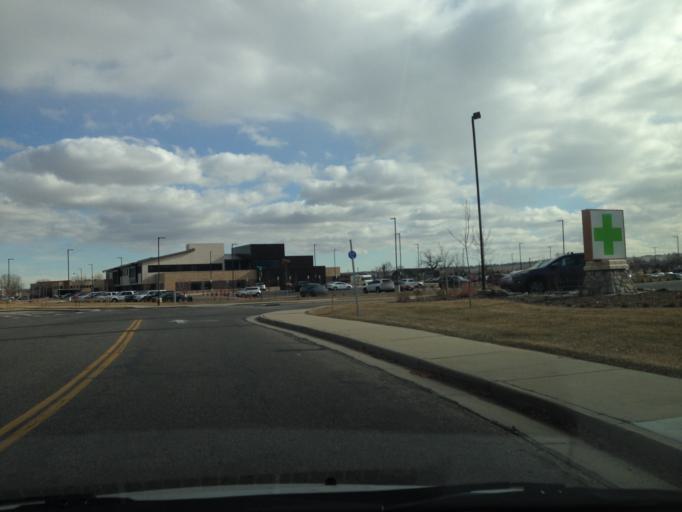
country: US
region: Colorado
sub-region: Boulder County
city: Lafayette
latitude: 39.9834
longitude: -105.0935
